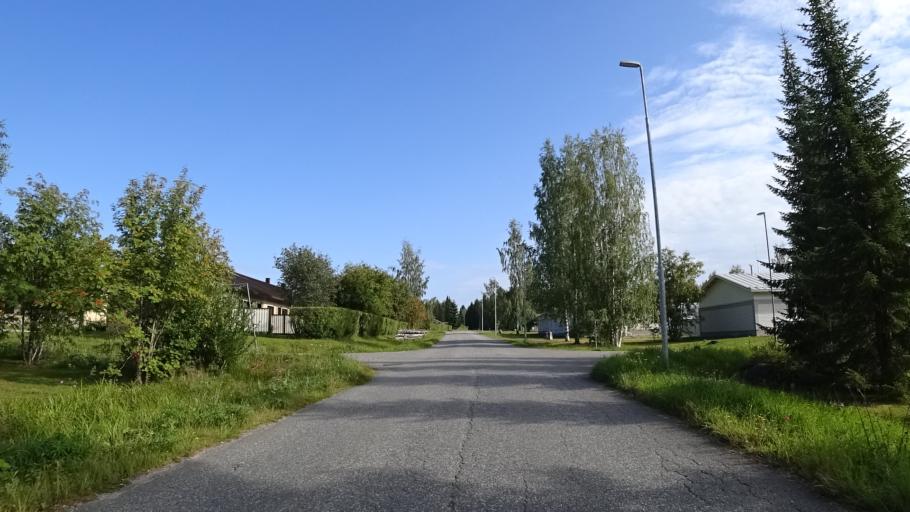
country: FI
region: North Karelia
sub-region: Joensuu
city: Eno
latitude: 62.7953
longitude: 30.1397
